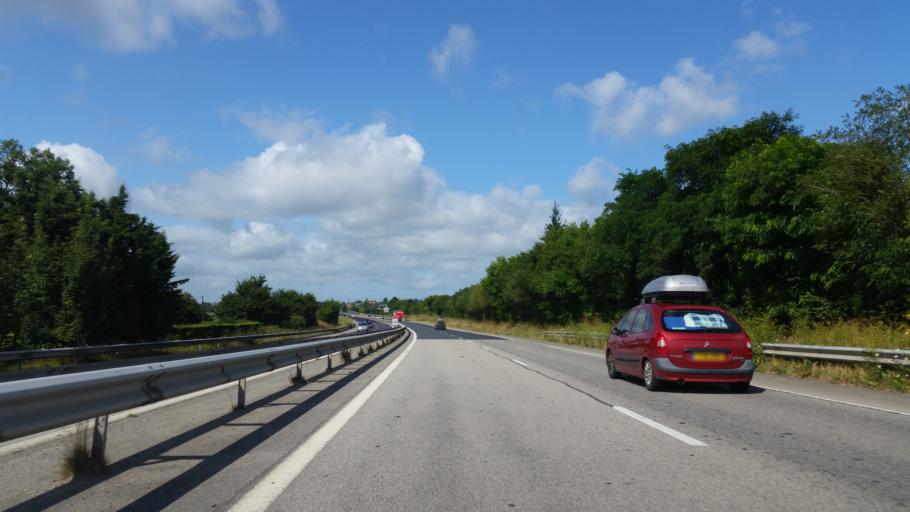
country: FR
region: Lower Normandy
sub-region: Departement du Calvados
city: Isigny-sur-Mer
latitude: 49.3083
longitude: -1.1305
